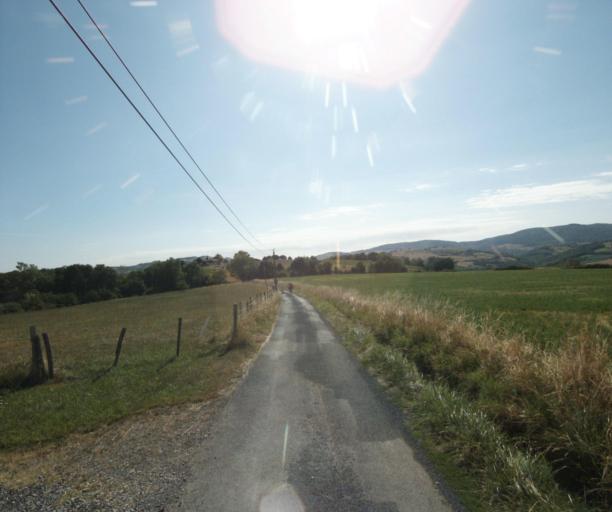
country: FR
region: Rhone-Alpes
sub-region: Departement du Rhone
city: Savigny
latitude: 45.8044
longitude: 4.5767
